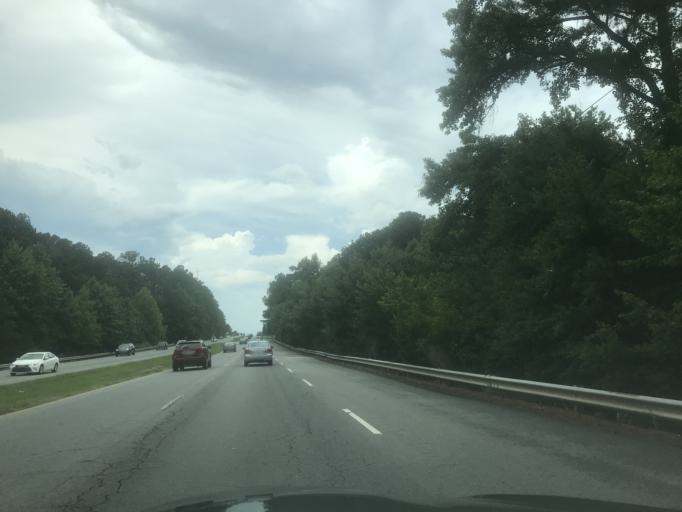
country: US
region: North Carolina
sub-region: Johnston County
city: Clayton
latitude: 35.6585
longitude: -78.4818
